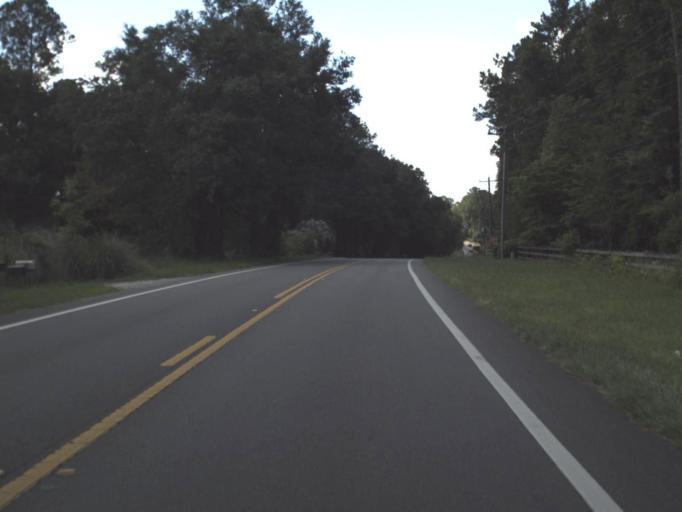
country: US
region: Florida
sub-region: Clay County
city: Keystone Heights
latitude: 29.6953
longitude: -82.0403
